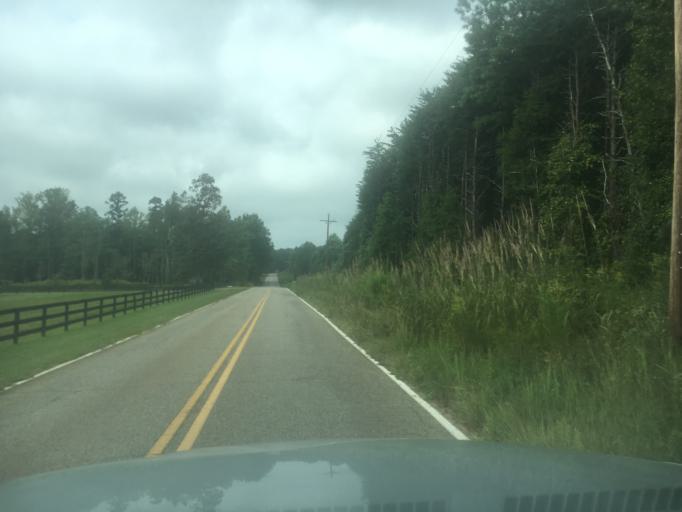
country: US
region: South Carolina
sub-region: Spartanburg County
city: Landrum
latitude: 35.1731
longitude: -82.0601
